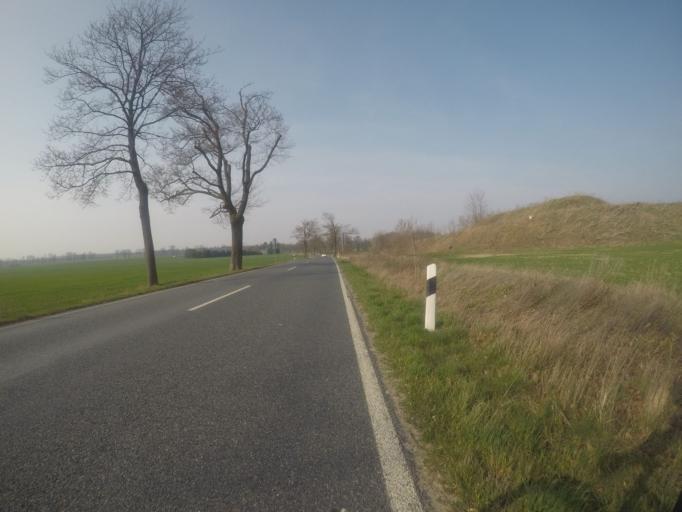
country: DE
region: Brandenburg
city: Schonefeld
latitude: 52.3294
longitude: 13.5027
